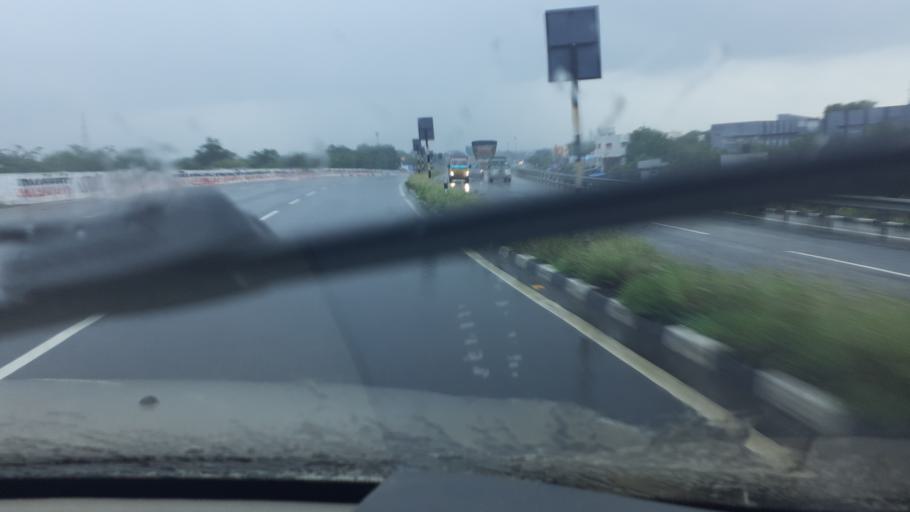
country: IN
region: Tamil Nadu
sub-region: Virudhunagar
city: Virudunagar
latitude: 9.6006
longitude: 77.9540
